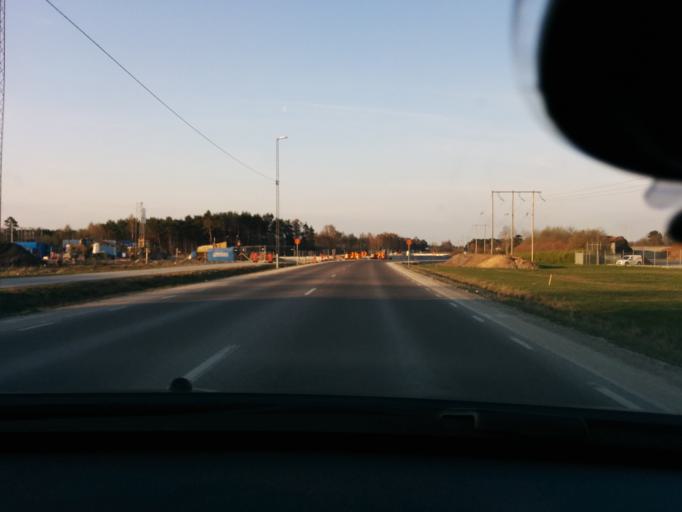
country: SE
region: Gotland
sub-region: Gotland
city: Visby
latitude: 57.6232
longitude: 18.3202
